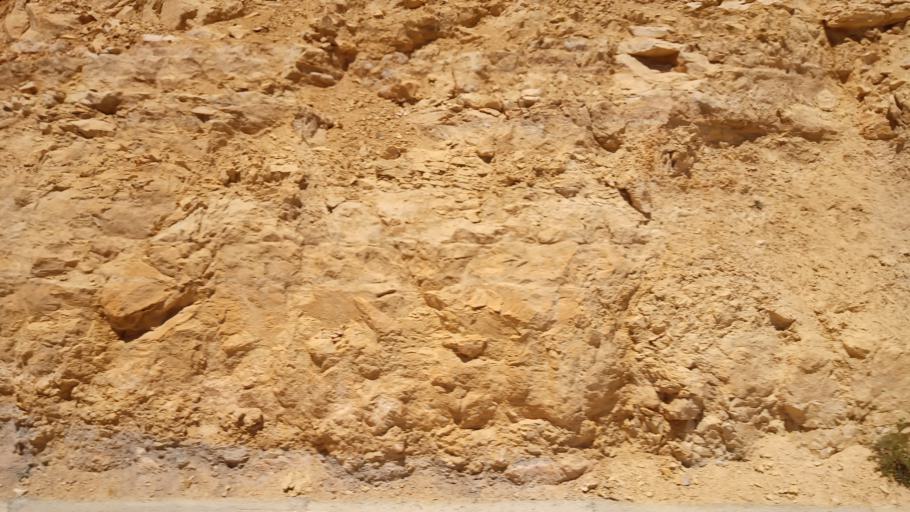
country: TR
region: Malatya
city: Darende
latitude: 38.6258
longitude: 37.4556
